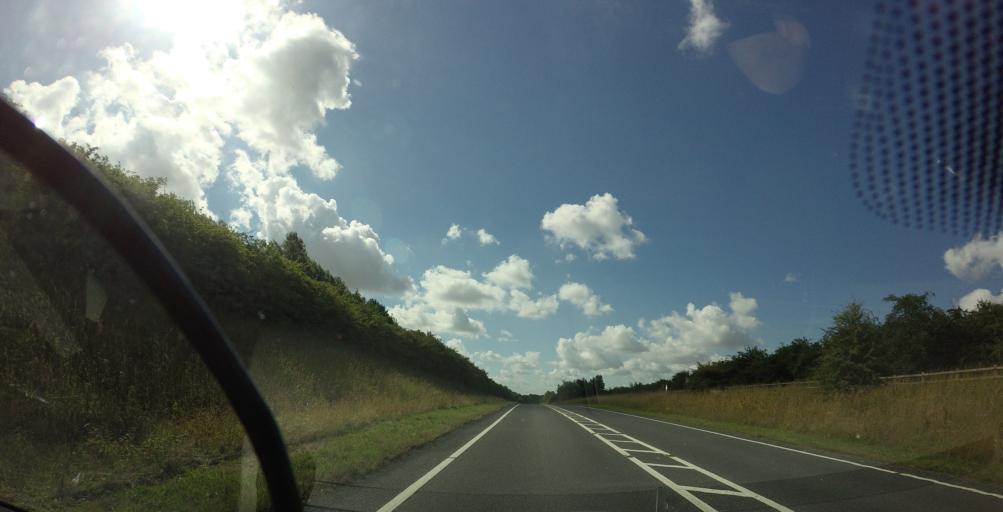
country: GB
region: England
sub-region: North Yorkshire
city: Boroughbridge
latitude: 54.0325
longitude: -1.3840
